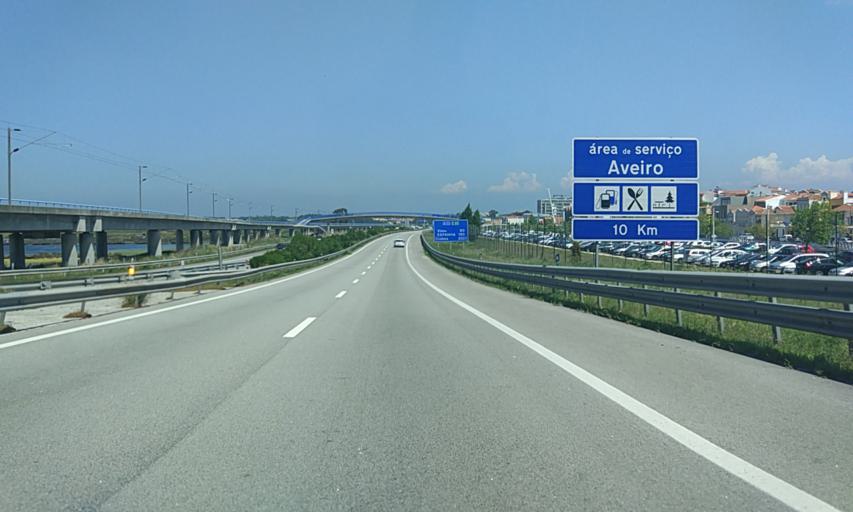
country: PT
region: Aveiro
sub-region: Aveiro
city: Aveiro
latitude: 40.6441
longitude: -8.6571
